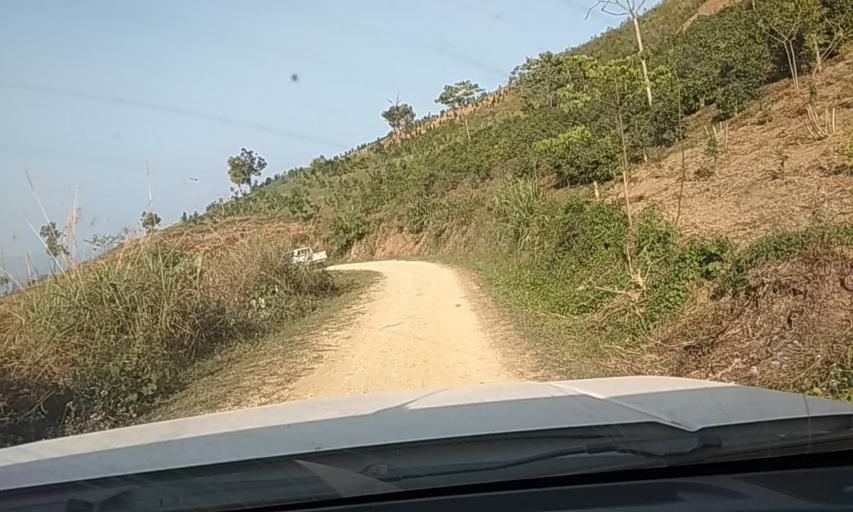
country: LA
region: Phongsali
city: Phongsali
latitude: 21.6679
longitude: 102.1820
